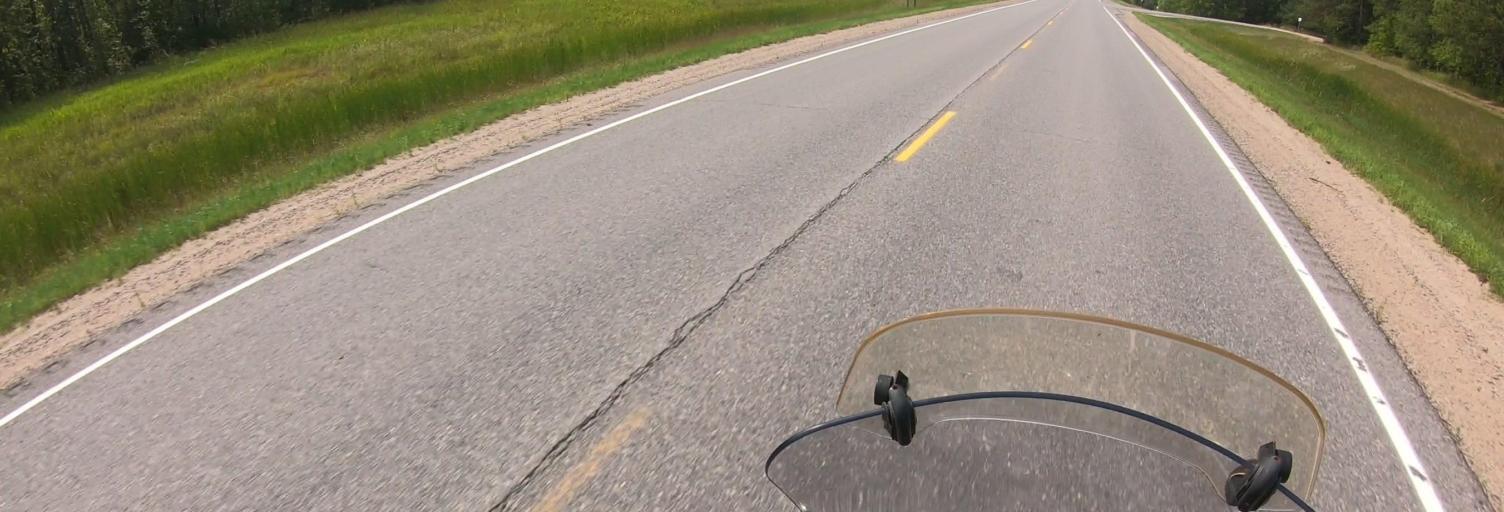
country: US
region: Minnesota
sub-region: Koochiching County
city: International Falls
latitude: 48.5219
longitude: -93.5825
